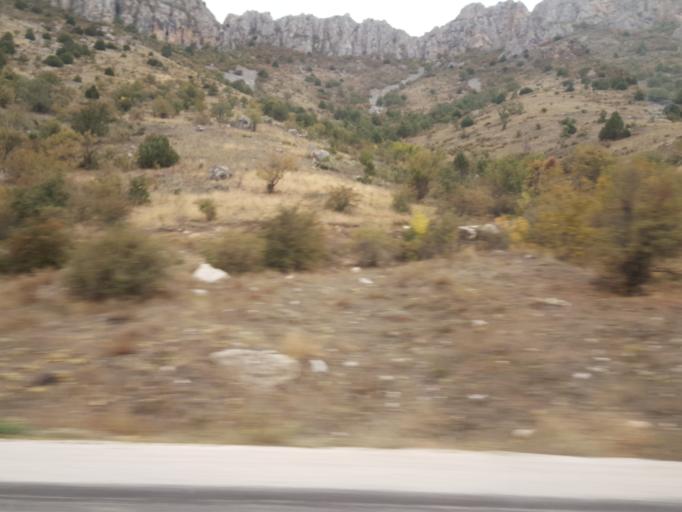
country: TR
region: Yozgat
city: Cekerek
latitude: 40.2095
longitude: 35.4884
